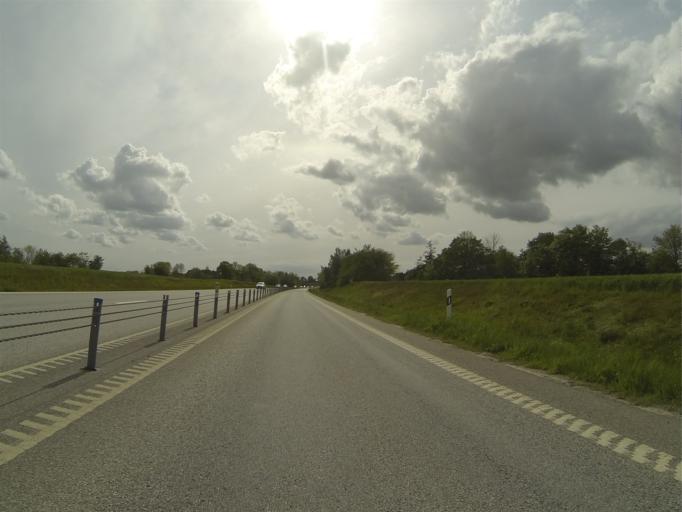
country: SE
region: Skane
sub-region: Lunds Kommun
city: Genarp
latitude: 55.6496
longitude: 13.3921
